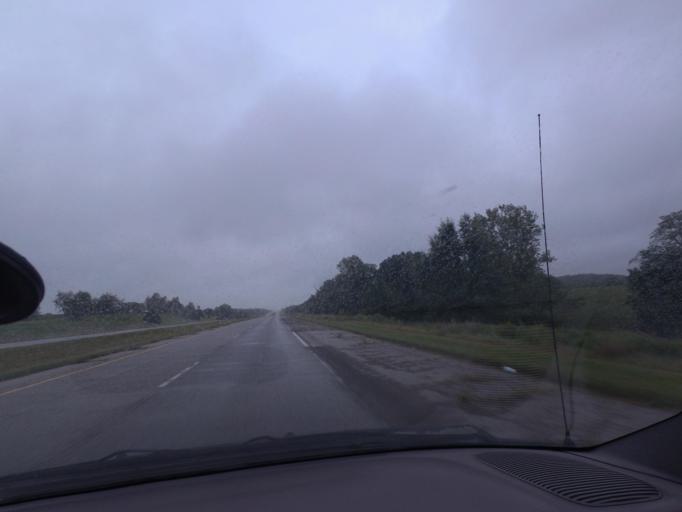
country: US
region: Illinois
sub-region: Pike County
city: Barry
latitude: 39.6927
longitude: -90.9471
